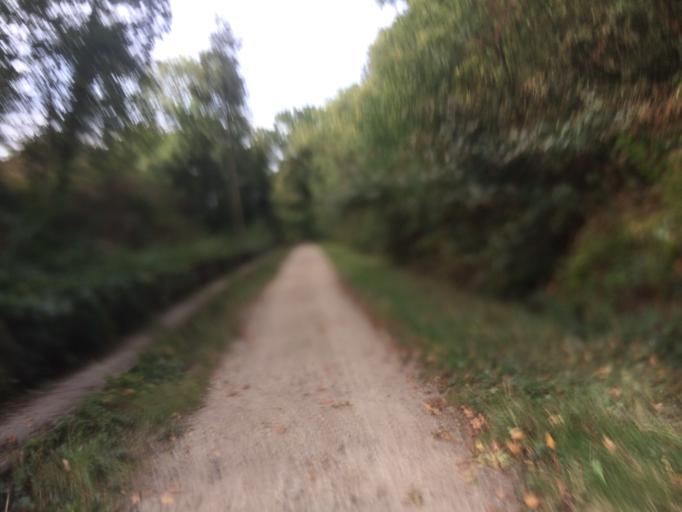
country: FR
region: Ile-de-France
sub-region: Departement de l'Essonne
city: Limours
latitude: 48.6504
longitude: 2.0690
